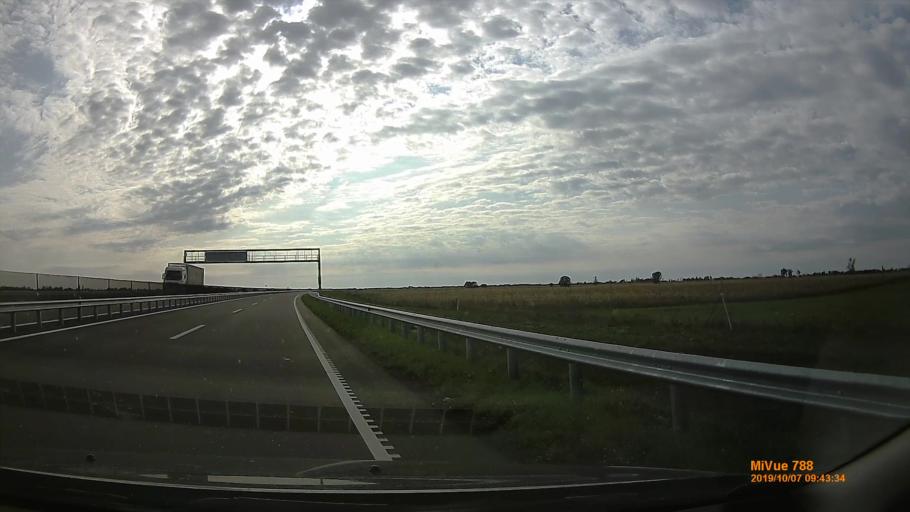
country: HU
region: Bekes
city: Kondoros
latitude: 46.8047
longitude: 20.6915
